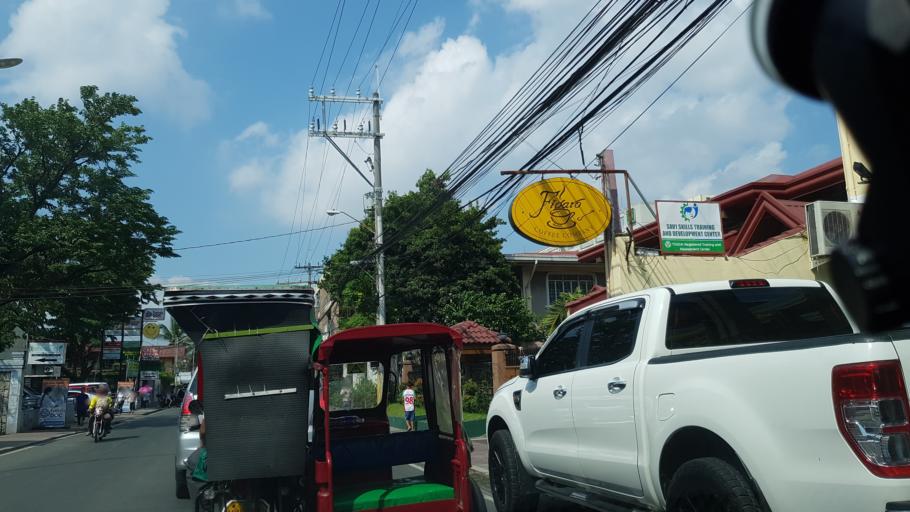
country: PH
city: Sambayanihan People's Village
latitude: 14.4694
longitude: 121.0212
